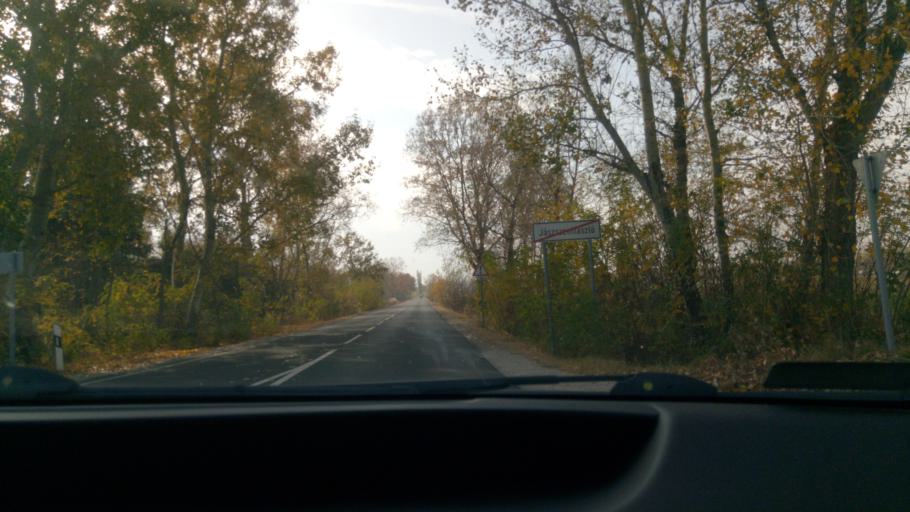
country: HU
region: Bacs-Kiskun
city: Jaszszentlaszlo
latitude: 46.5655
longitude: 19.7514
